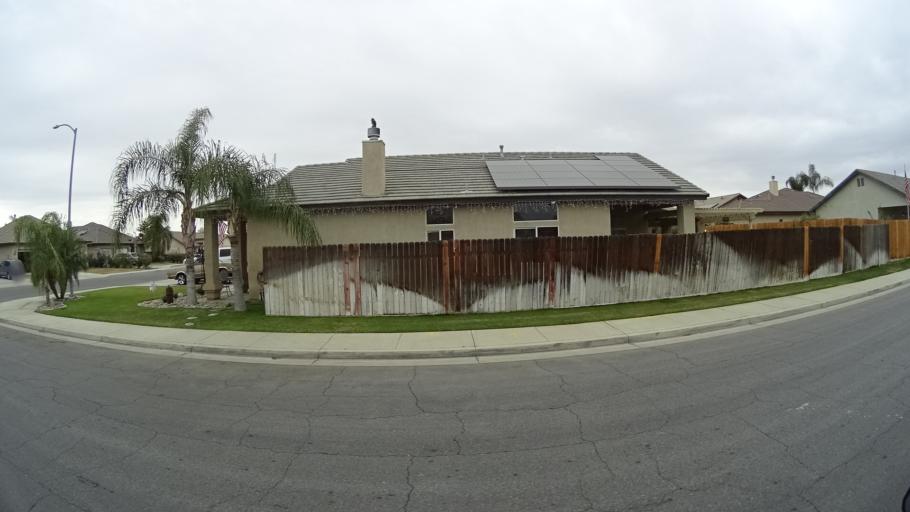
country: US
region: California
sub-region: Kern County
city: Greenfield
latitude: 35.2880
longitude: -119.0340
